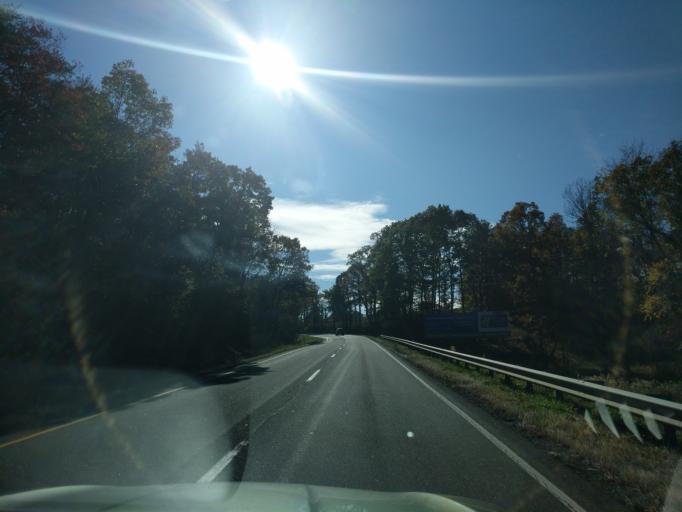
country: US
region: Virginia
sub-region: Frederick County
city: Shawnee Land
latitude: 39.2994
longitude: -78.2792
